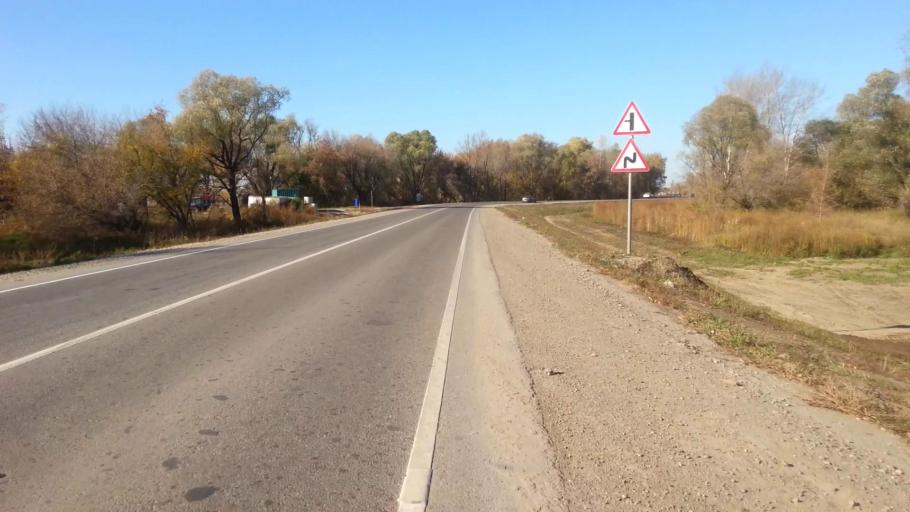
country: RU
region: Altai Krai
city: Sannikovo
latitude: 53.3210
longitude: 83.9434
